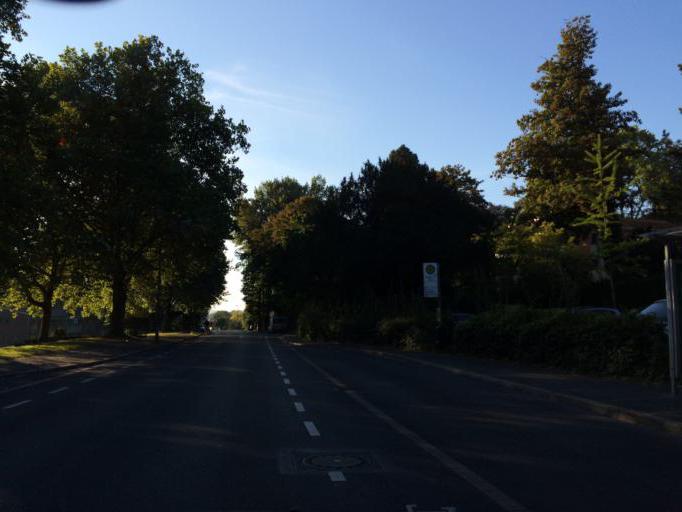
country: DE
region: North Rhine-Westphalia
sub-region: Regierungsbezirk Koln
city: Konigswinter
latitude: 50.6790
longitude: 7.1564
